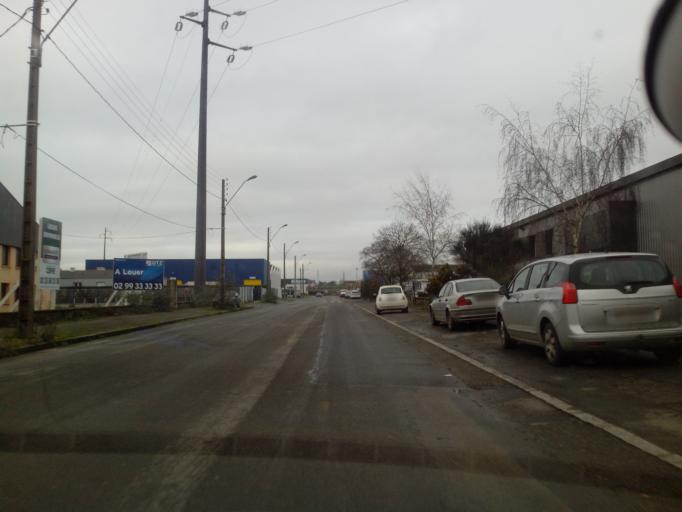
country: FR
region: Brittany
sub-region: Departement d'Ille-et-Vilaine
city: Vezin-le-Coquet
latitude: 48.1050
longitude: -1.7257
